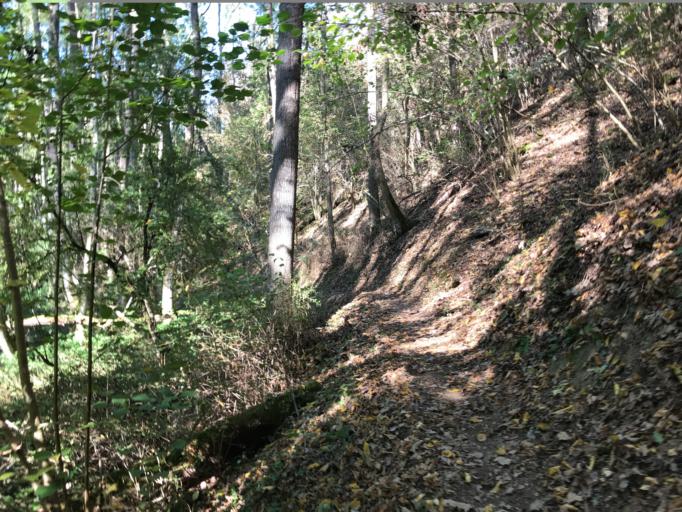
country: DE
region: Rheinland-Pfalz
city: Kobern-Gondorf
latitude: 50.2997
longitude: 7.4293
